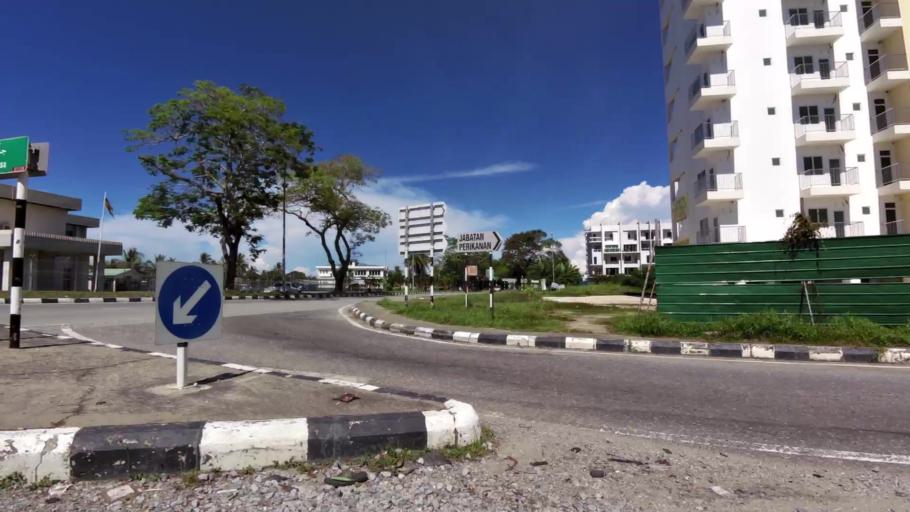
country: BN
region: Brunei and Muara
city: Bandar Seri Begawan
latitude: 5.0296
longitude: 115.0620
